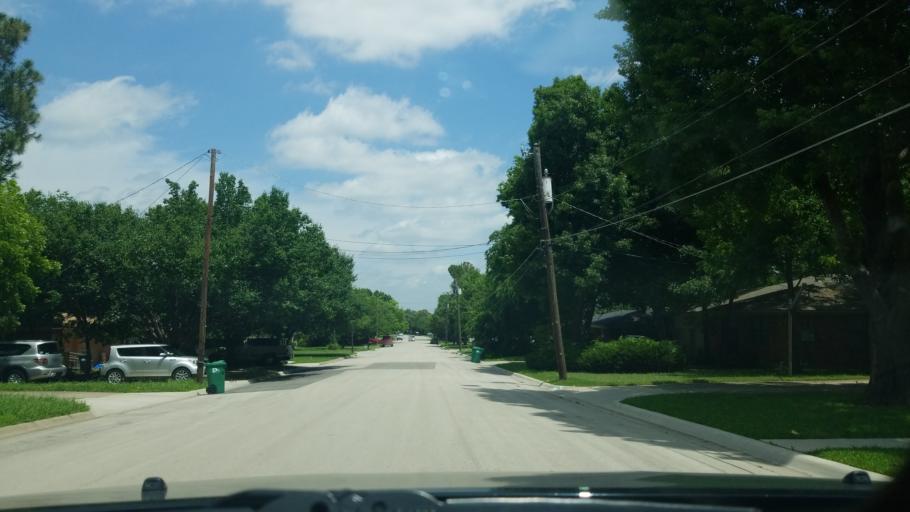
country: US
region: Texas
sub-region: Denton County
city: Denton
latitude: 33.2230
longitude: -97.1599
